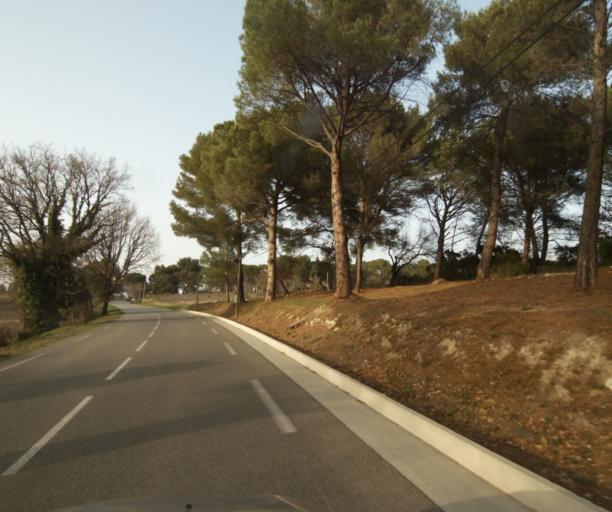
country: FR
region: Provence-Alpes-Cote d'Azur
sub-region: Departement des Bouches-du-Rhone
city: Eguilles
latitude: 43.5915
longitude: 5.3674
